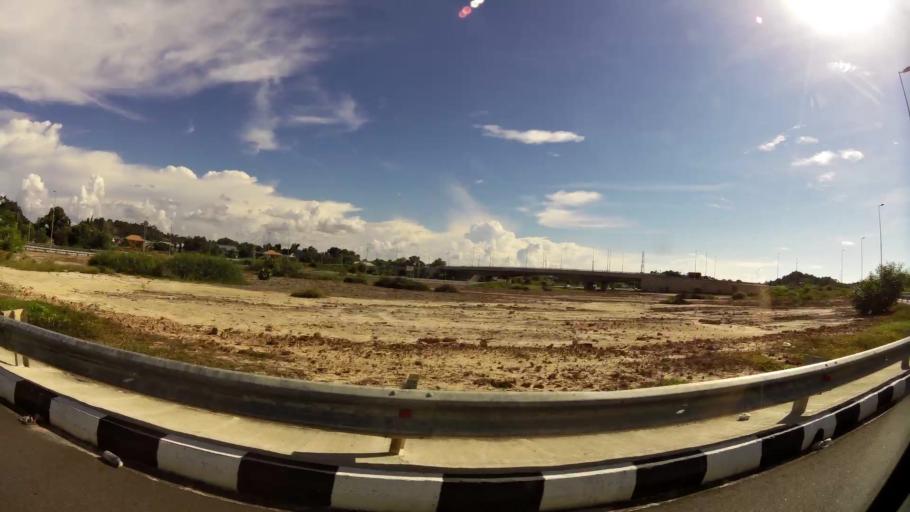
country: BN
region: Brunei and Muara
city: Bandar Seri Begawan
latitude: 4.9879
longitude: 114.9619
